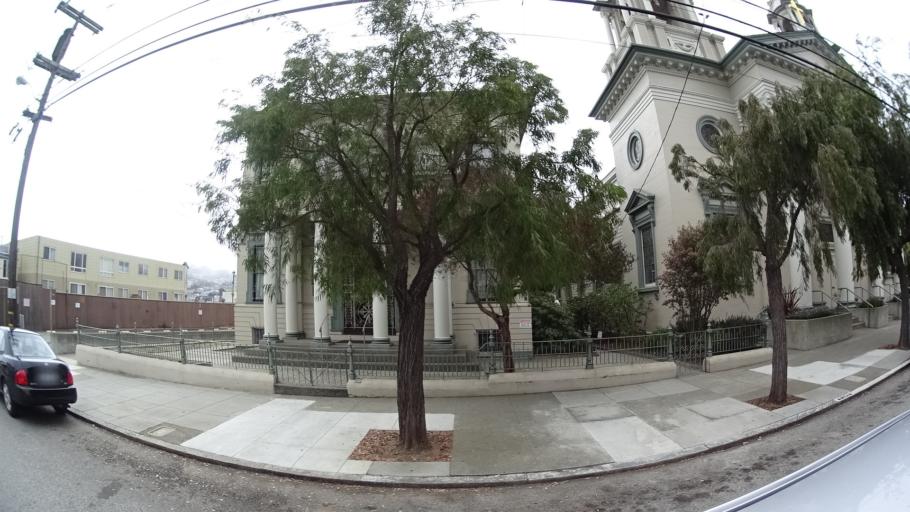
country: US
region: California
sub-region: San Francisco County
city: San Francisco
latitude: 37.7344
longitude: -122.4271
